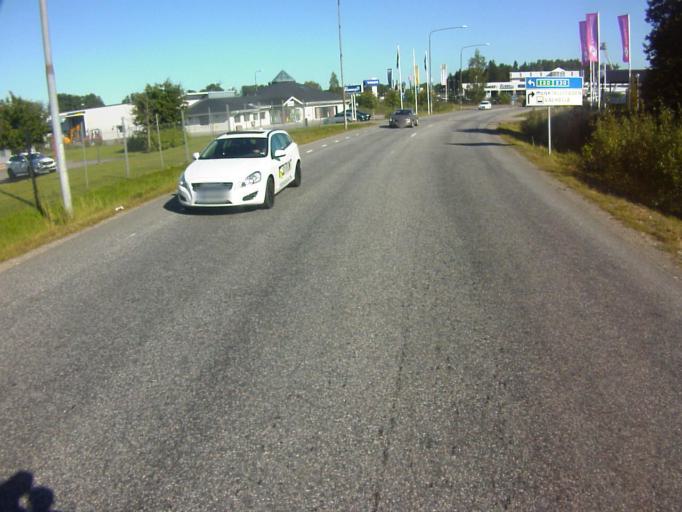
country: SE
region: Soedermanland
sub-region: Eskilstuna Kommun
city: Torshalla
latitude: 59.3864
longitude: 16.4680
